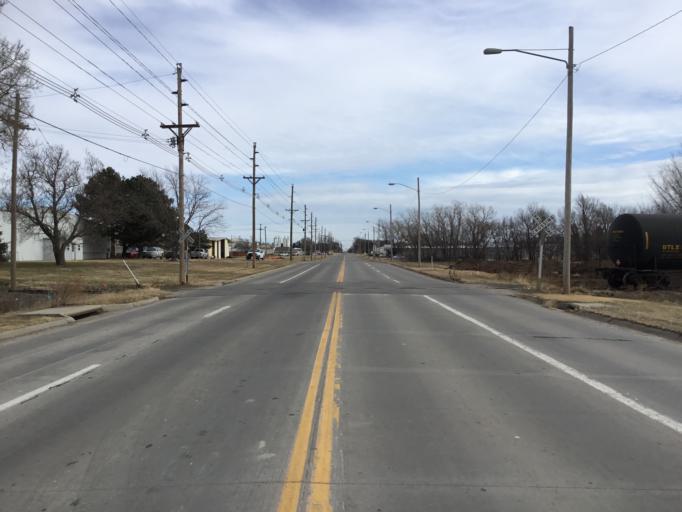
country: US
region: Kansas
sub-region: McPherson County
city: McPherson
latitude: 38.3767
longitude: -97.6809
